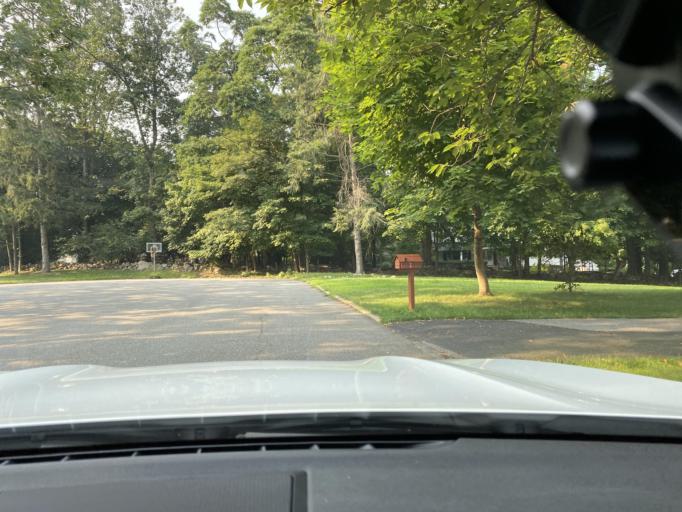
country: US
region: New York
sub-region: Rockland County
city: Airmont
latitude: 41.0979
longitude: -74.1296
